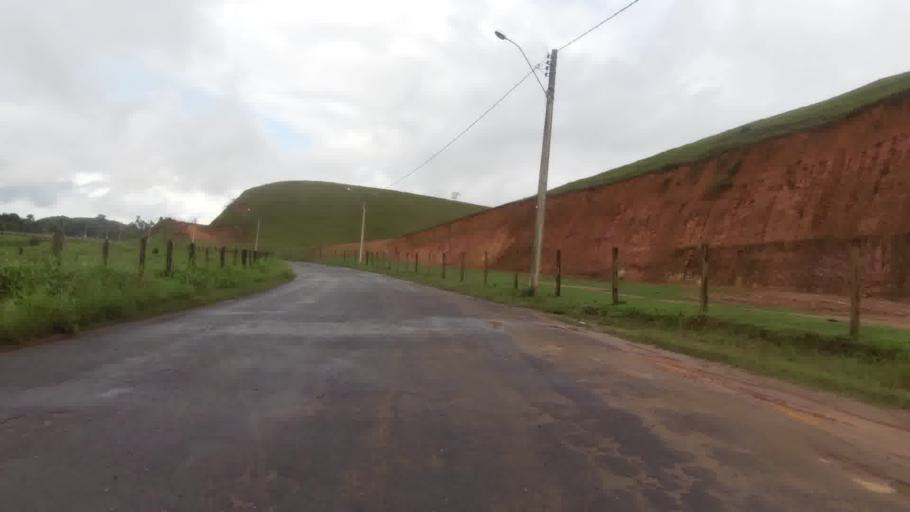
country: BR
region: Espirito Santo
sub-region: Alfredo Chaves
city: Alfredo Chaves
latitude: -20.6891
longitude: -40.6818
